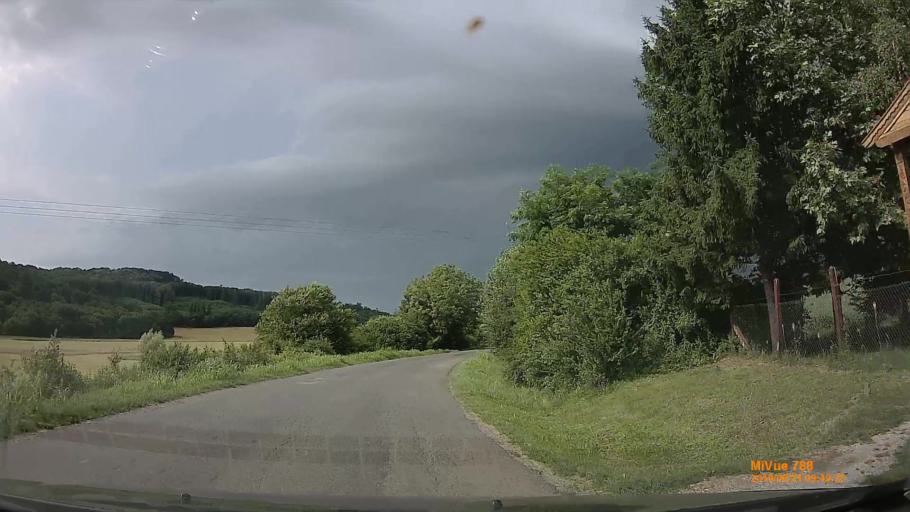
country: HU
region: Baranya
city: Sasd
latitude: 46.2682
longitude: 18.0381
